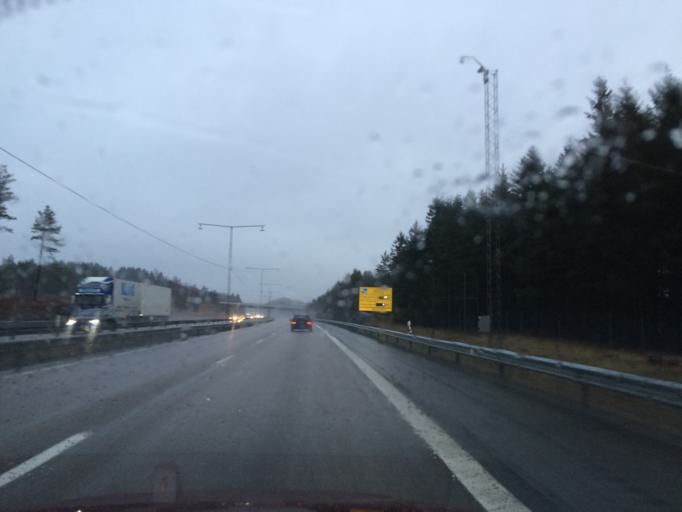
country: SE
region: Vaestra Goetaland
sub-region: Molndal
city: Lindome
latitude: 57.5691
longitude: 12.0567
